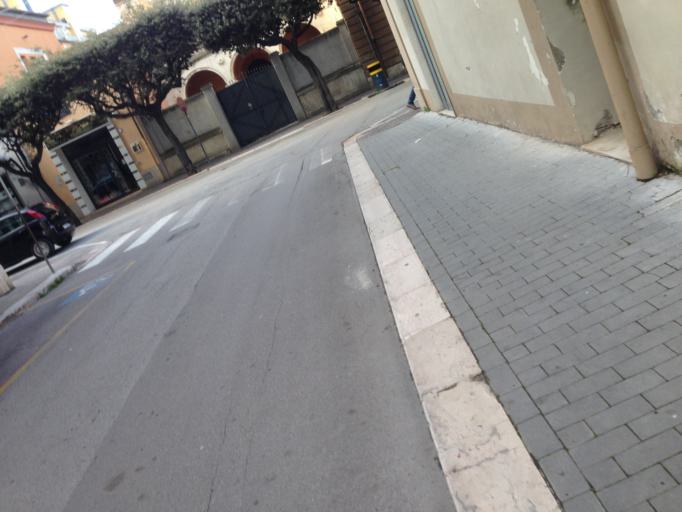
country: IT
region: Molise
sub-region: Provincia di Campobasso
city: Termoli
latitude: 42.0001
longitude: 14.9958
